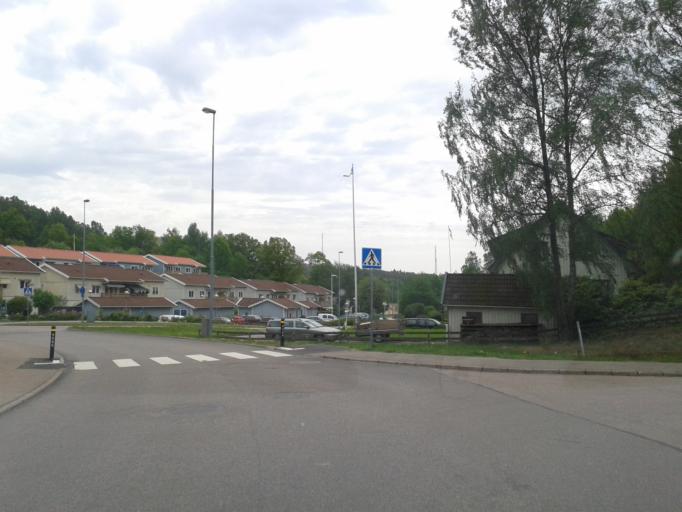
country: SE
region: Vaestra Goetaland
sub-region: Kungalvs Kommun
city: Kungalv
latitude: 57.8868
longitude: 11.9527
